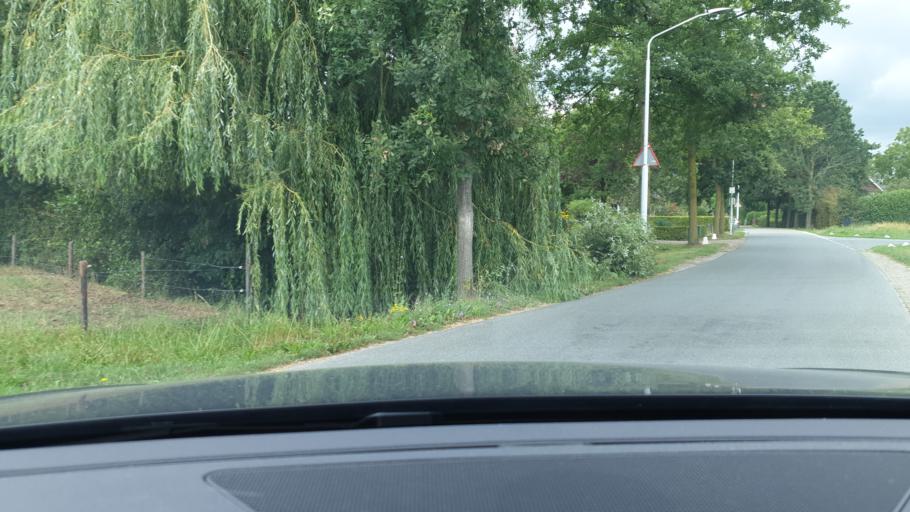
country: NL
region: North Brabant
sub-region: Gemeente Best
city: Best
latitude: 51.5142
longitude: 5.3791
